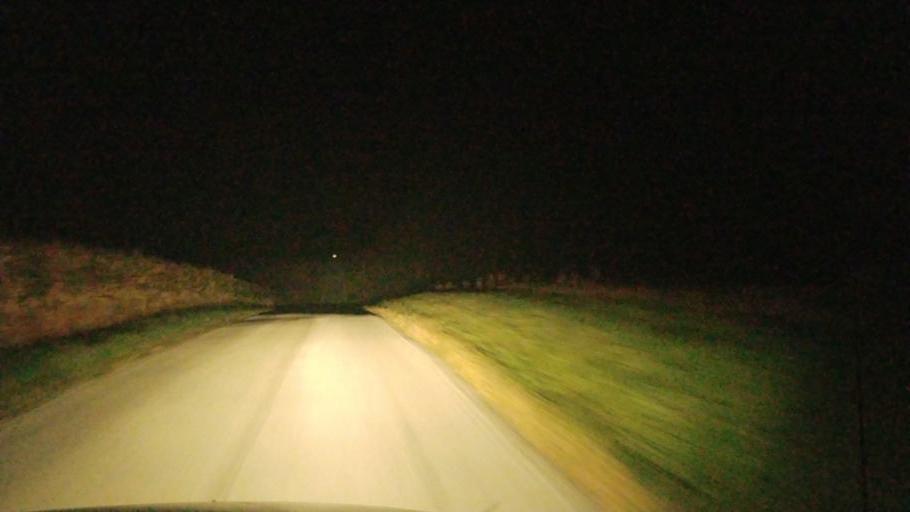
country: US
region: Ohio
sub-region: Highland County
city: Leesburg
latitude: 39.3080
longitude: -83.5629
